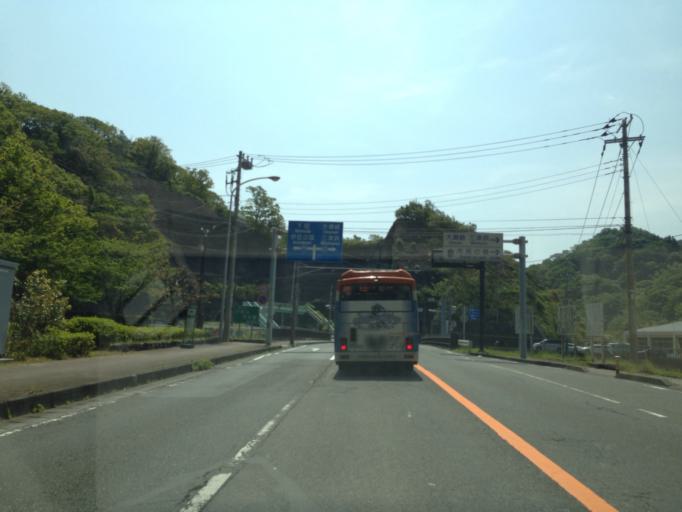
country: JP
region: Shizuoka
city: Numazu
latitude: 35.0489
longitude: 138.9058
